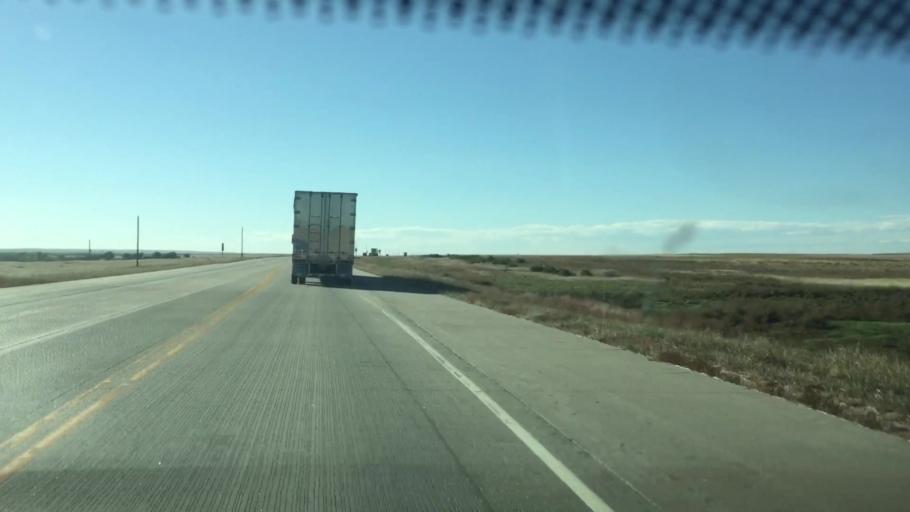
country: US
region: Colorado
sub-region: Kiowa County
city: Eads
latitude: 38.8267
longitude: -103.0169
